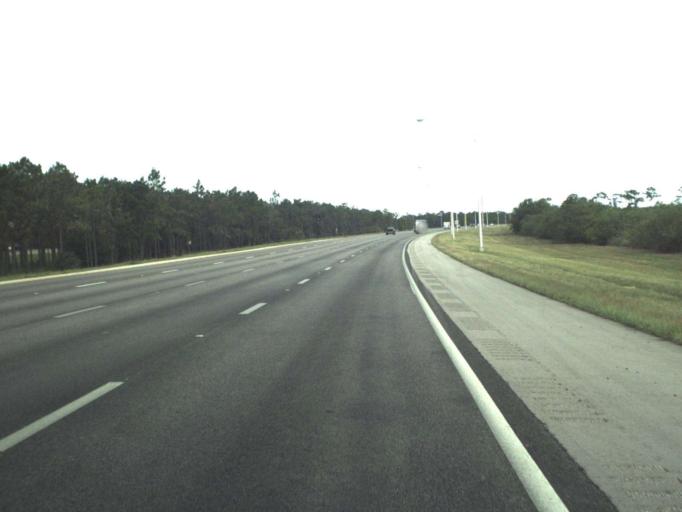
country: US
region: Florida
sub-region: Saint Lucie County
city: Lakewood Park
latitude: 27.4726
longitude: -80.4283
